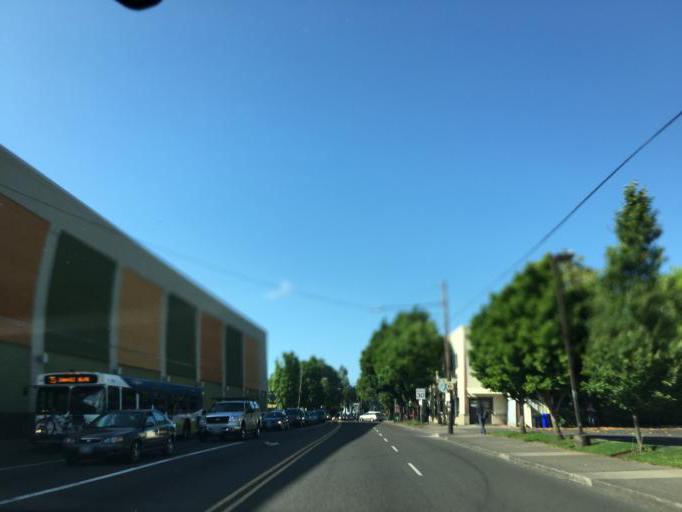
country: US
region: Oregon
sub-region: Multnomah County
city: Portland
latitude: 45.5121
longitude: -122.6228
